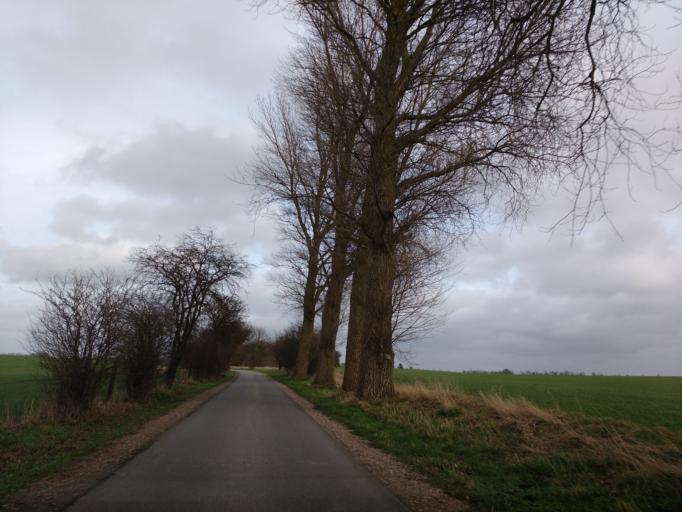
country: DE
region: Schleswig-Holstein
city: Gremersdorf
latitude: 54.3642
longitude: 10.9362
